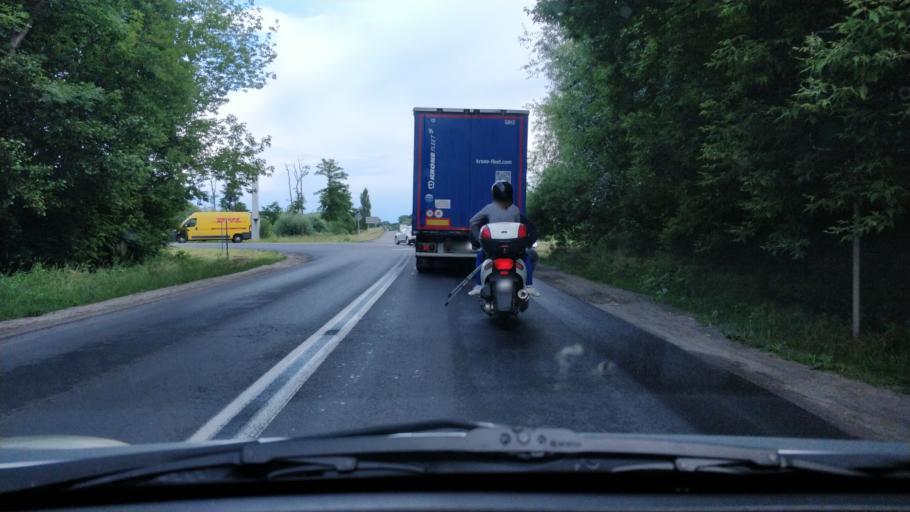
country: PL
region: Greater Poland Voivodeship
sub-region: Powiat poznanski
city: Daszewice
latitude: 52.3193
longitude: 17.0245
